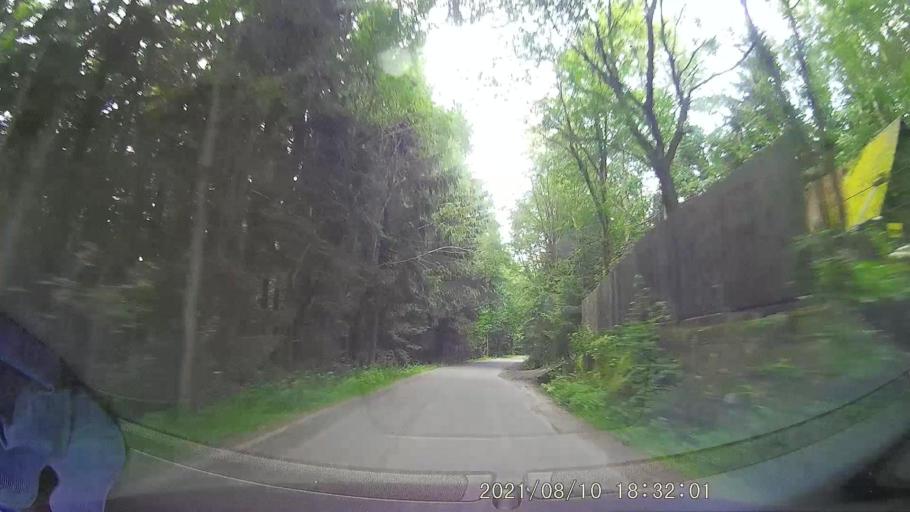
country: CZ
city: Machov
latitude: 50.4873
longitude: 16.3370
